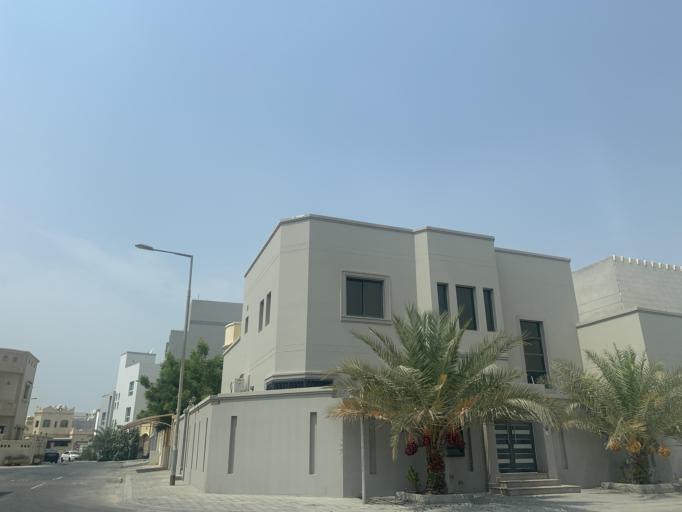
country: BH
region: Manama
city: Jidd Hafs
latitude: 26.2093
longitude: 50.5088
